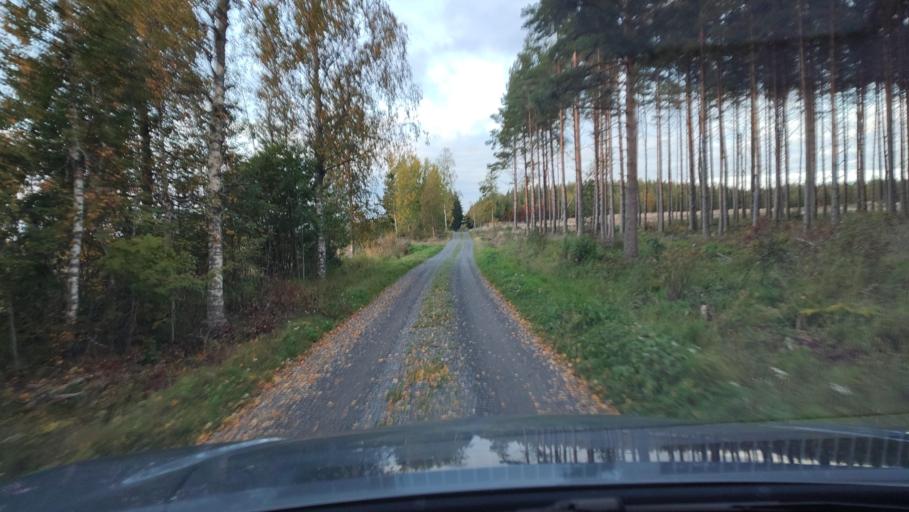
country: FI
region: Ostrobothnia
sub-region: Sydosterbotten
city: Kristinestad
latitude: 62.2481
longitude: 21.4537
